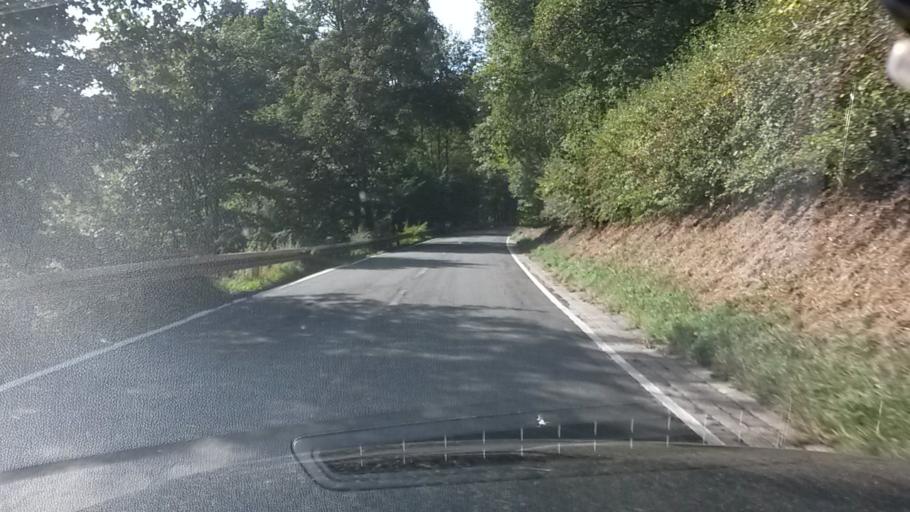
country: DE
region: North Rhine-Westphalia
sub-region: Regierungsbezirk Arnsberg
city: Luedenscheid
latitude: 51.1947
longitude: 7.6768
